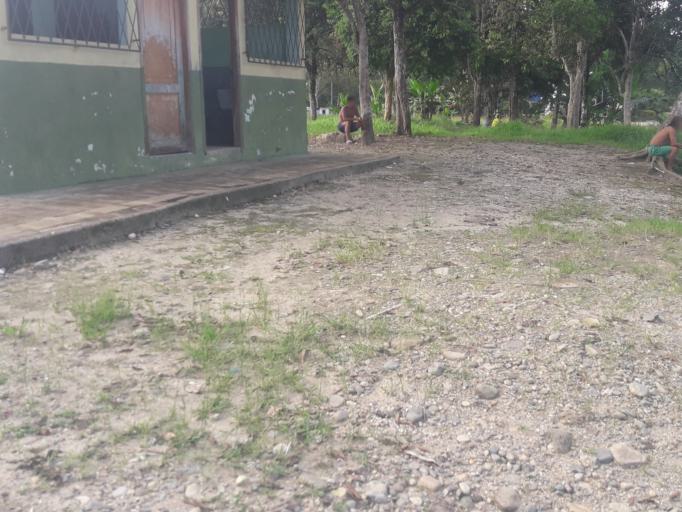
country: EC
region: Napo
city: Tena
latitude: -0.9890
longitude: -77.8098
